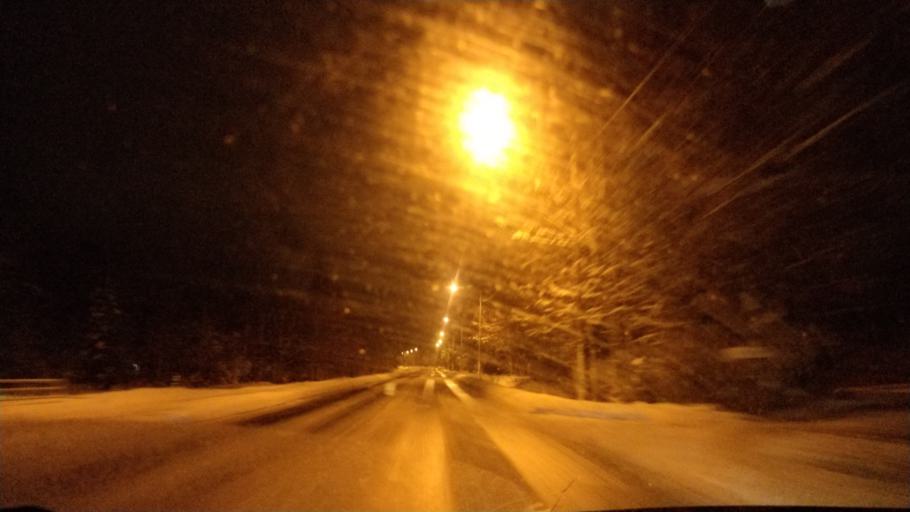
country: FI
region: Lapland
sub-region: Rovaniemi
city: Rovaniemi
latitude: 66.3830
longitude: 25.3780
